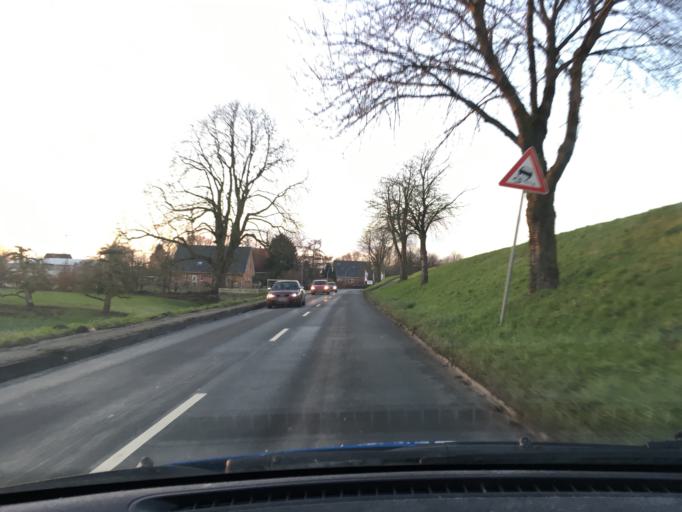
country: DE
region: Hamburg
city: Altona
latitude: 53.5006
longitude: 9.8822
